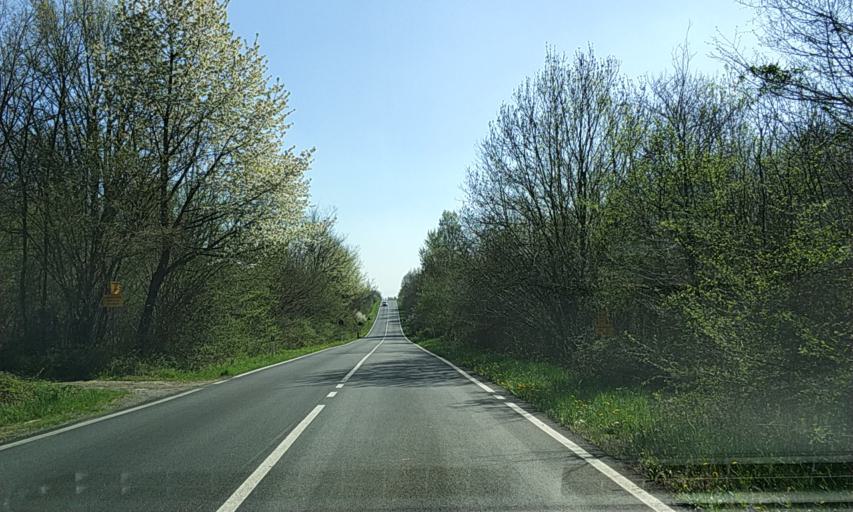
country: IT
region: Piedmont
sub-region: Provincia di Torino
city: Grosso
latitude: 45.2745
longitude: 7.5815
